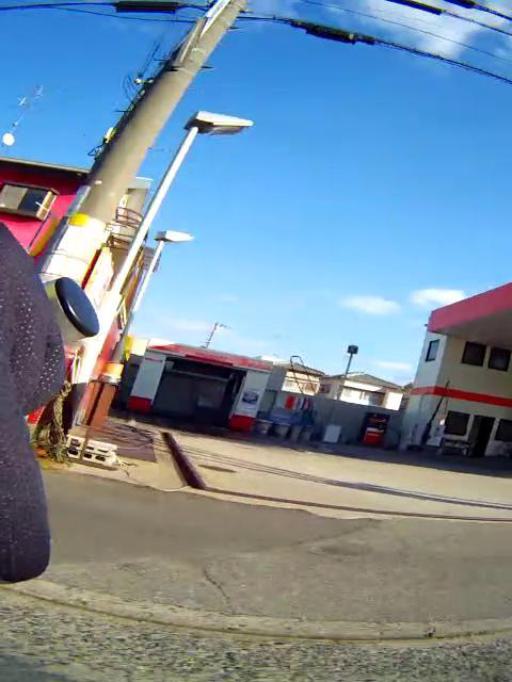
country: JP
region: Hyogo
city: Takarazuka
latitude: 34.7853
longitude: 135.3583
